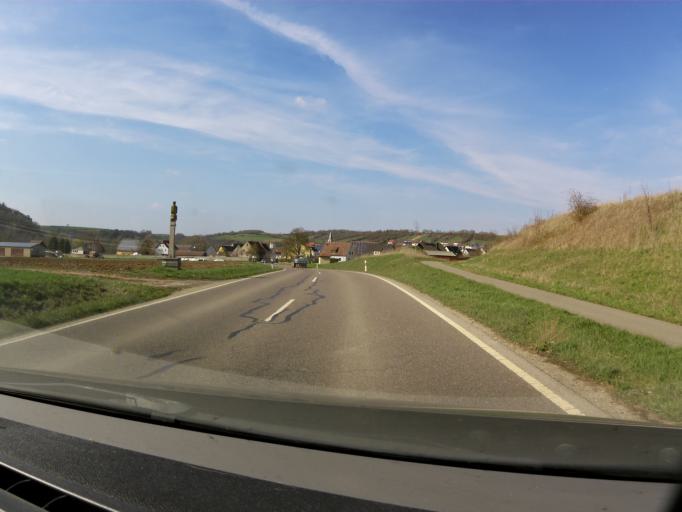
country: DE
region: Bavaria
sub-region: Regierungsbezirk Unterfranken
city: Bieberehren
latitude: 49.5115
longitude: 10.0104
